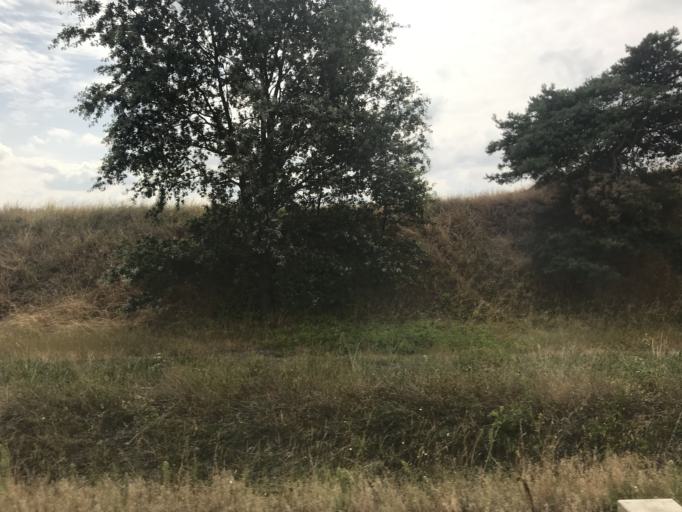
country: PL
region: Greater Poland Voivodeship
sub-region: Powiat gnieznienski
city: Trzemeszno
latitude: 52.5440
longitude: 17.7346
